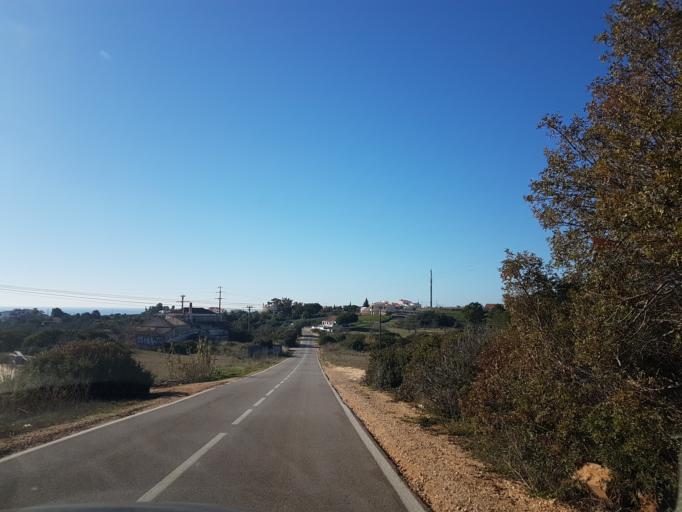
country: PT
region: Faro
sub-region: Lagoa
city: Carvoeiro
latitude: 37.1007
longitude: -8.4162
